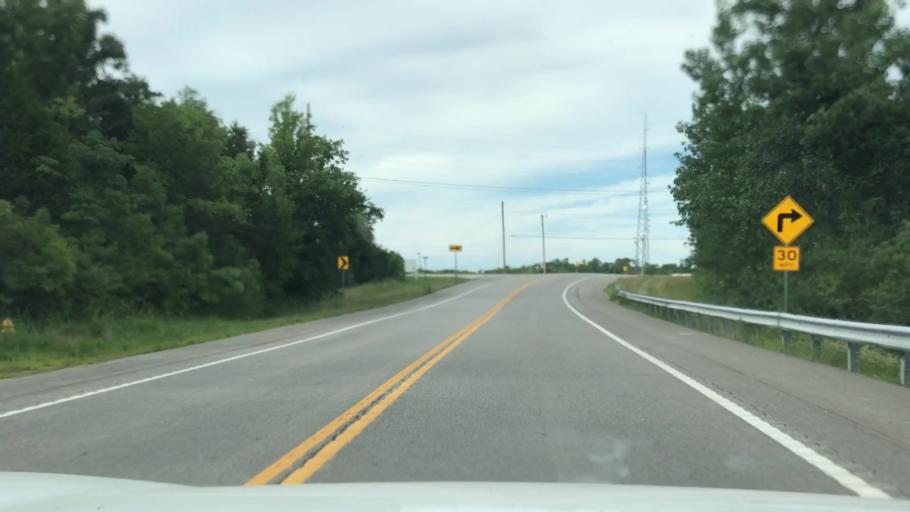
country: US
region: Missouri
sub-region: Saint Charles County
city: Weldon Spring
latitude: 38.6941
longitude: -90.7242
